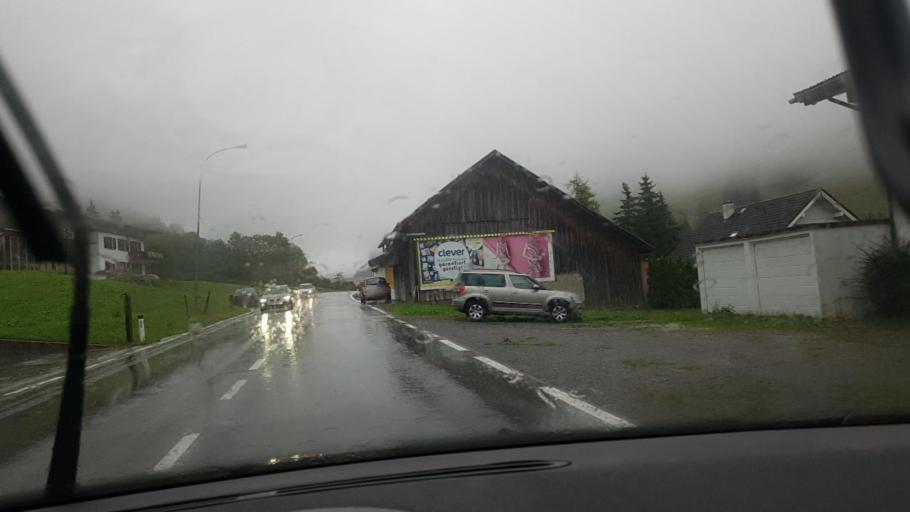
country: AT
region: Vorarlberg
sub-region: Politischer Bezirk Bludenz
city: Klosterle
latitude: 47.1309
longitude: 10.0606
